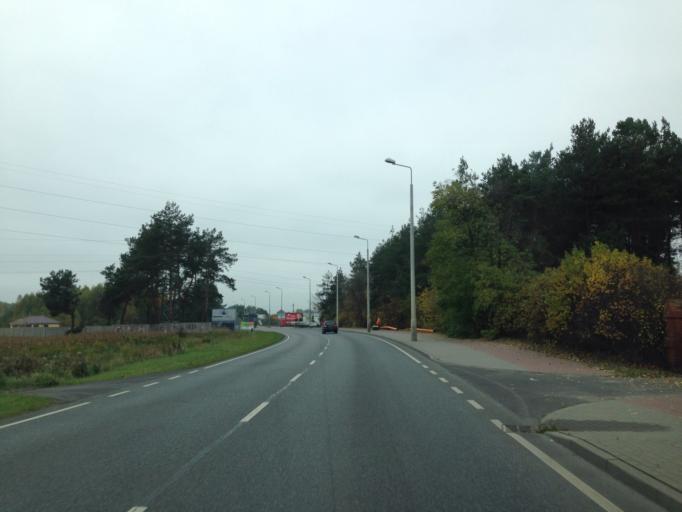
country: PL
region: Kujawsko-Pomorskie
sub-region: Grudziadz
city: Grudziadz
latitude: 53.4505
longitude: 18.8048
